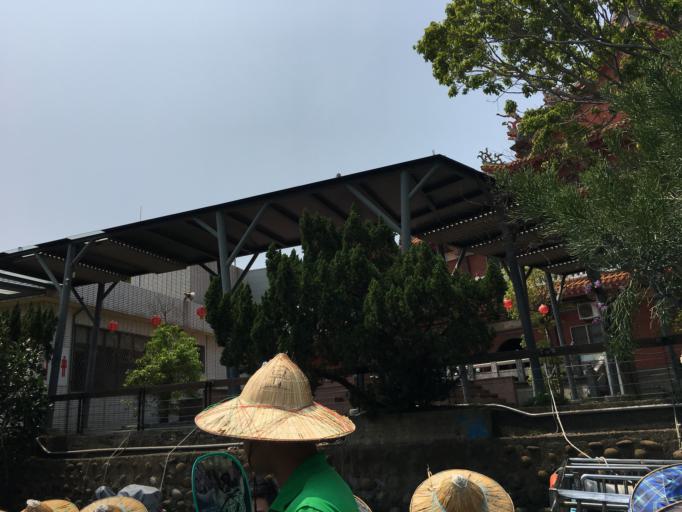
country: TW
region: Taiwan
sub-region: Tainan
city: Tainan
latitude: 23.0201
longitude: 120.1355
